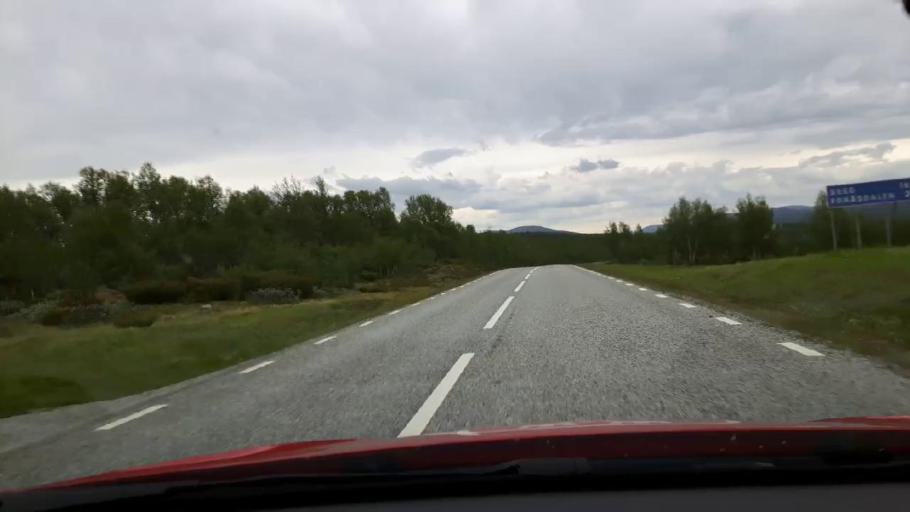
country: NO
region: Sor-Trondelag
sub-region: Tydal
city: Aas
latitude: 62.6309
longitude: 12.1213
